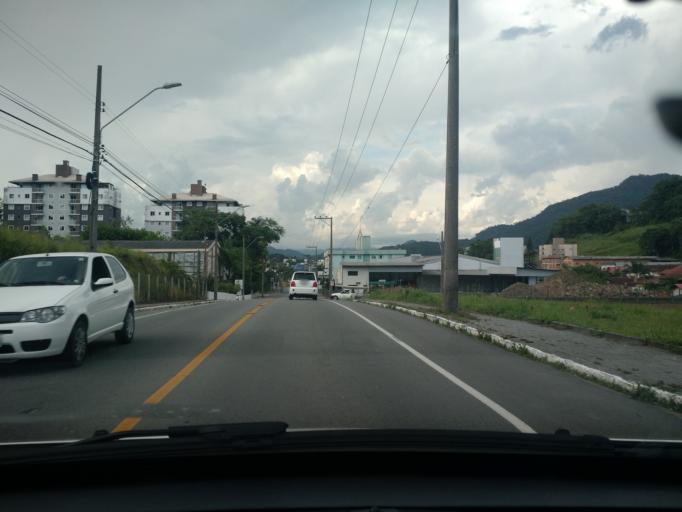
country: BR
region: Santa Catarina
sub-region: Jaragua Do Sul
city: Jaragua do Sul
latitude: -26.4899
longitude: -49.0915
